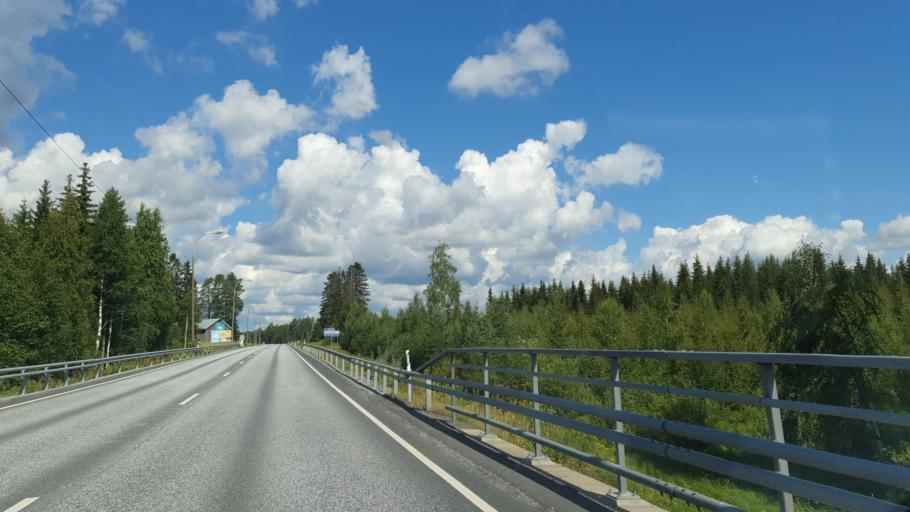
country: FI
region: Northern Savo
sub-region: Ylae-Savo
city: Sonkajaervi
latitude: 63.8760
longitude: 27.4405
